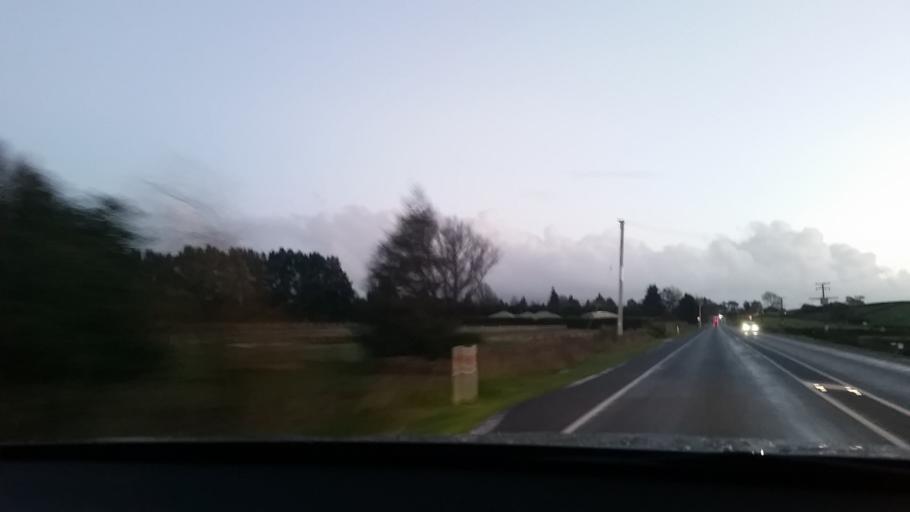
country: NZ
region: Waikato
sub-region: Hamilton City
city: Hamilton
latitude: -37.8103
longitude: 175.2363
